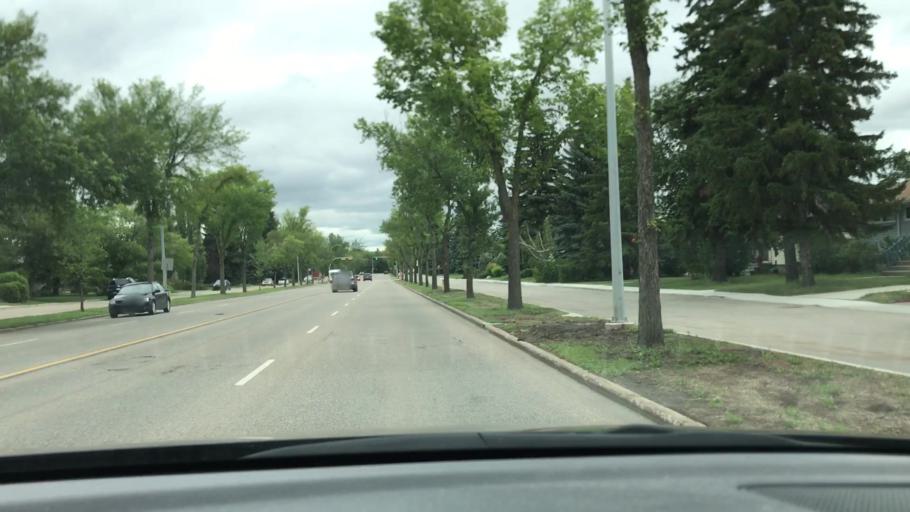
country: CA
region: Alberta
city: Edmonton
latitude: 53.5193
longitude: -113.5735
